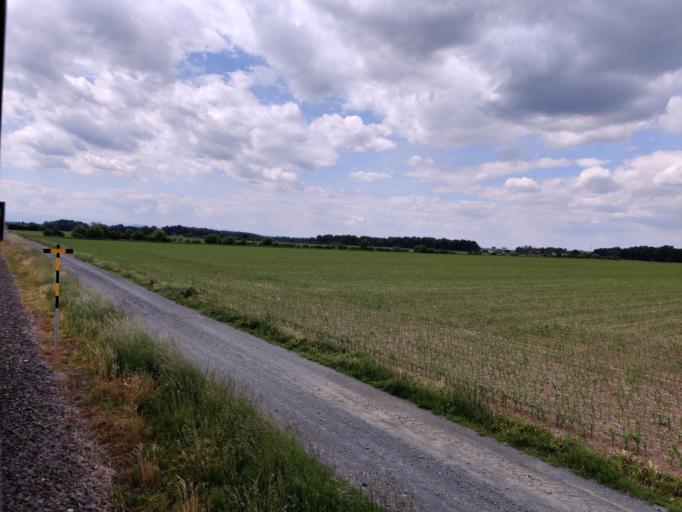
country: SI
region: Sentilj
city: Selnica ob Muri
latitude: 46.7141
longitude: 15.6975
